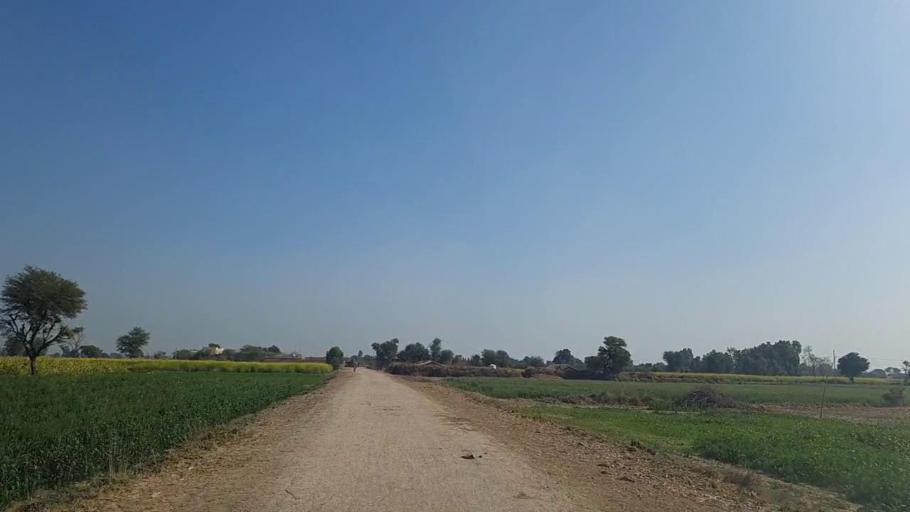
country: PK
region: Sindh
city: Shahpur Chakar
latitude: 26.1917
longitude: 68.6065
